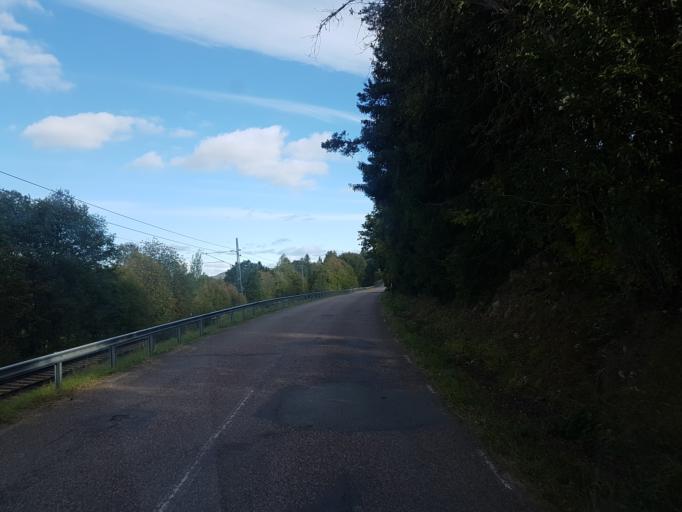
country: SE
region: Dalarna
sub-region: Saters Kommun
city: Saeter
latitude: 60.3642
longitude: 15.7274
